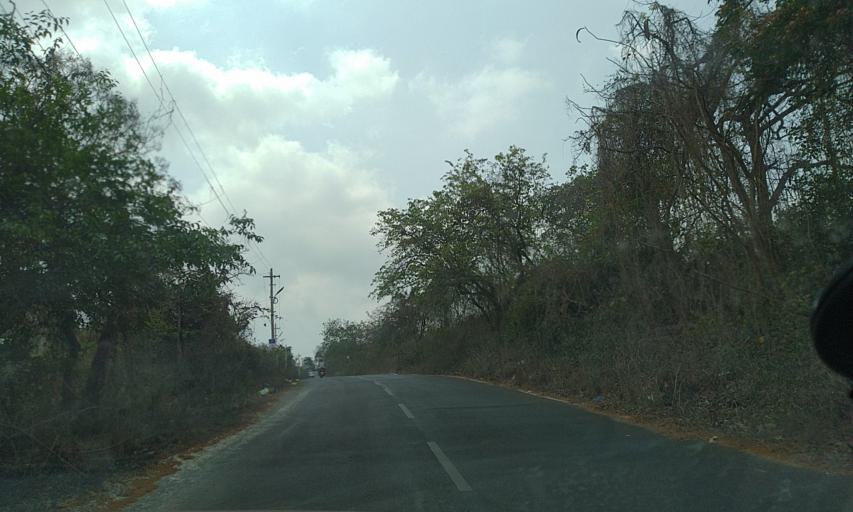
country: IN
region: Goa
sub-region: North Goa
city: Jua
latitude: 15.4926
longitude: 73.9110
